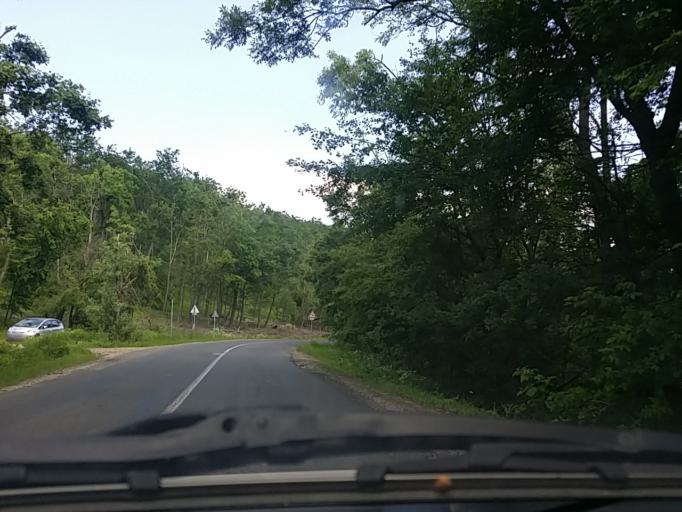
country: HU
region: Pest
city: Pilisszentkereszt
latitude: 47.7153
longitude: 18.8681
